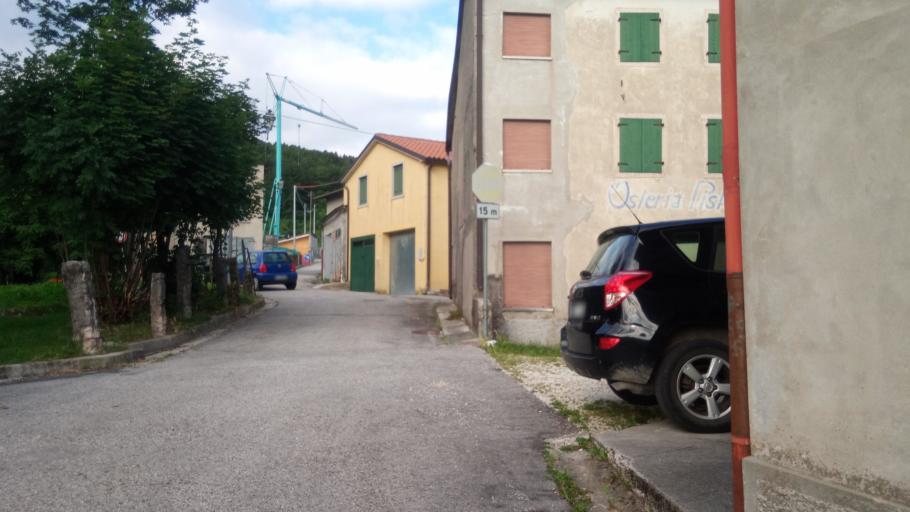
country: IT
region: Veneto
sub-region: Provincia di Vicenza
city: Conco
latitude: 45.8050
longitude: 11.6143
